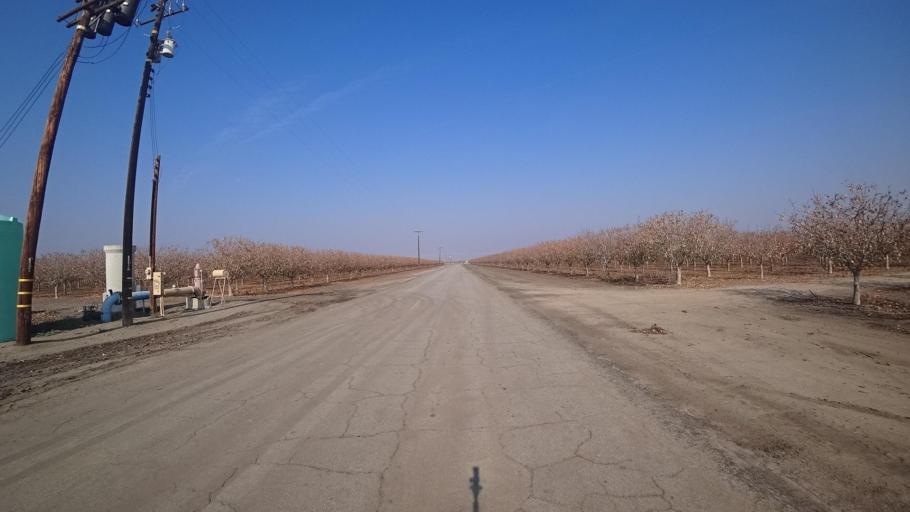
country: US
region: California
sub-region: Kern County
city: Buttonwillow
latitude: 35.3509
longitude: -119.3945
